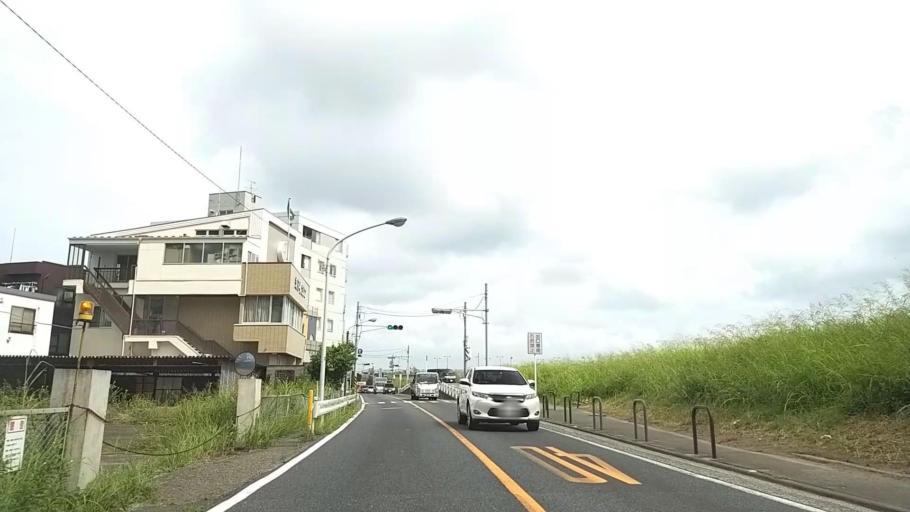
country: JP
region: Kanagawa
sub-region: Kawasaki-shi
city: Kawasaki
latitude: 35.5819
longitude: 139.6674
